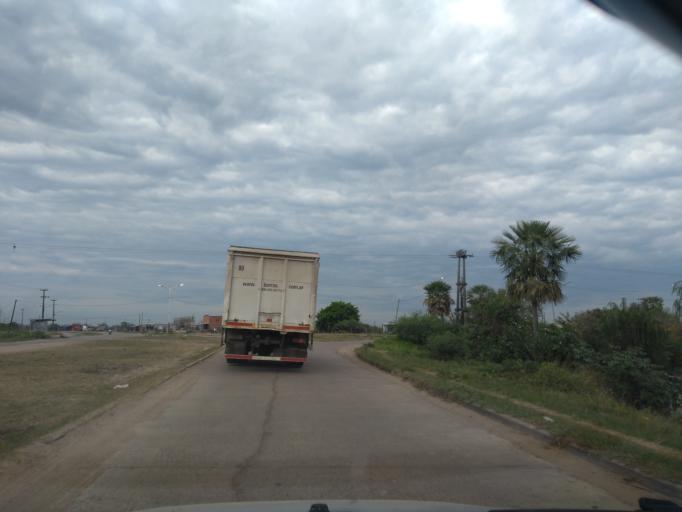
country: AR
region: Chaco
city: Puerto Vilelas
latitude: -27.5183
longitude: -58.9418
